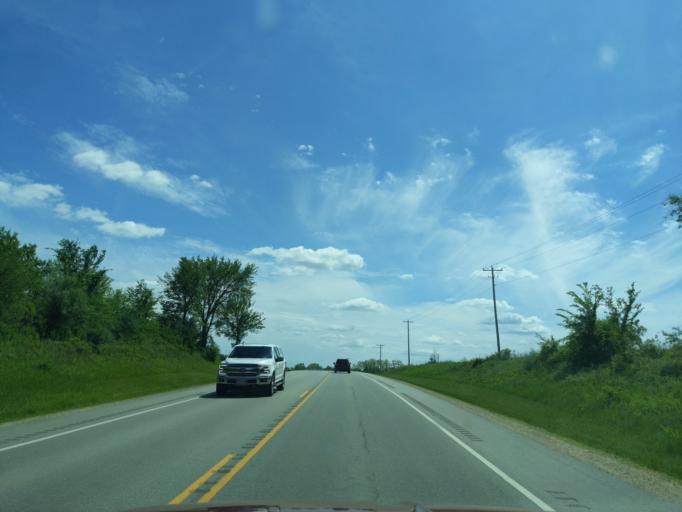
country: US
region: Wisconsin
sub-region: Columbia County
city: Rio
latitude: 43.4427
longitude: -89.3294
